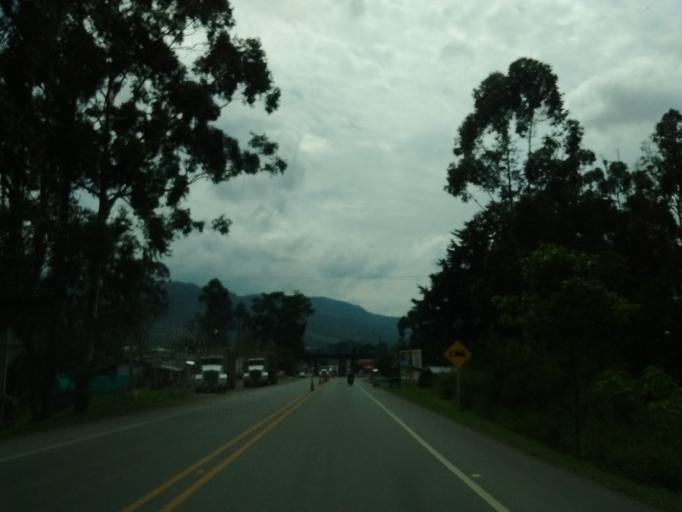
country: CO
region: Cauca
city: Cajibio
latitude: 2.7033
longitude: -76.5379
